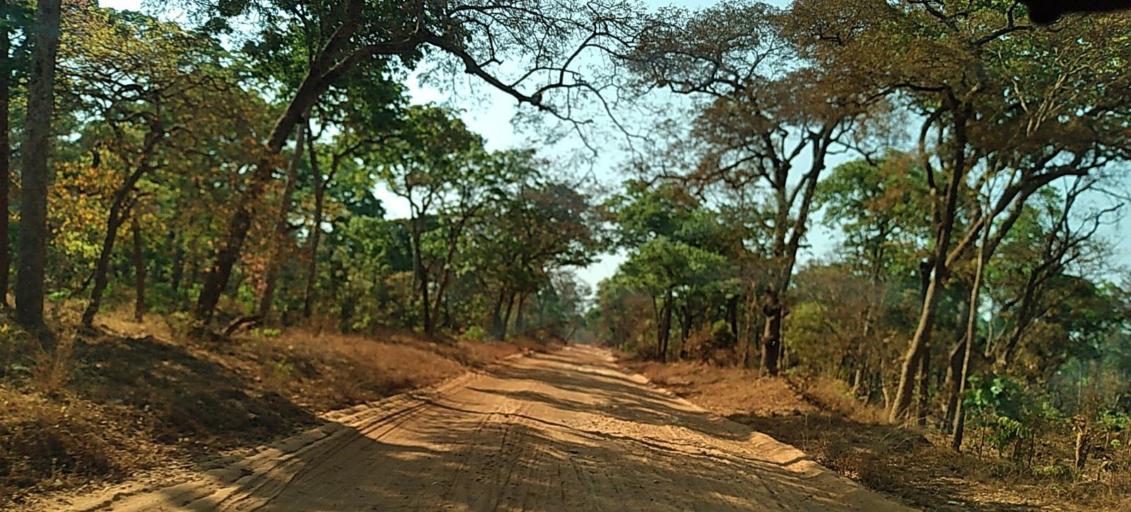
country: ZM
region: North-Western
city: Kasempa
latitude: -13.6699
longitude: 26.0153
